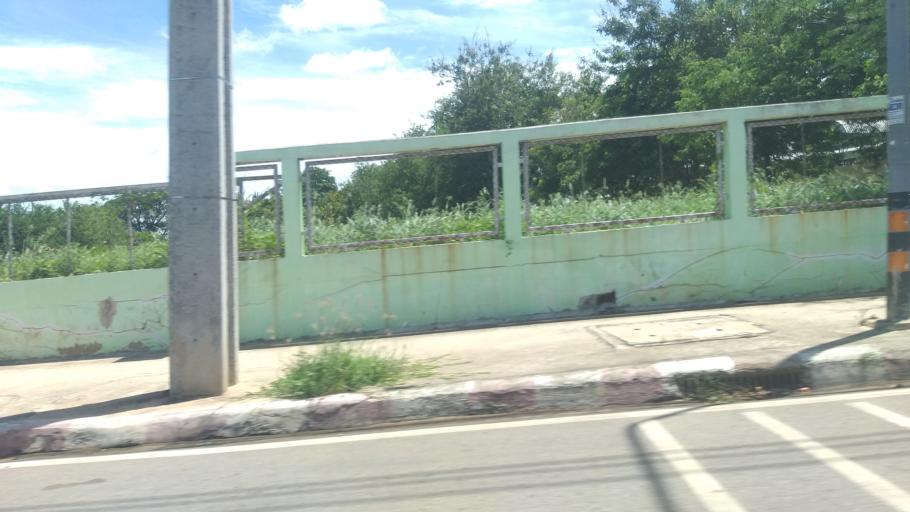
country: TH
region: Khon Kaen
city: Khon Kaen
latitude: 16.4327
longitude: 102.8201
